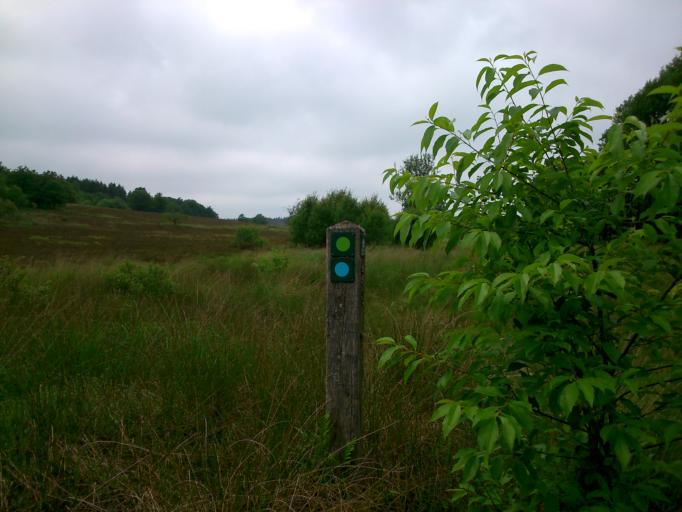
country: DK
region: Central Jutland
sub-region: Ringkobing-Skjern Kommune
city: Videbaek
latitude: 56.2197
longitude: 8.6149
